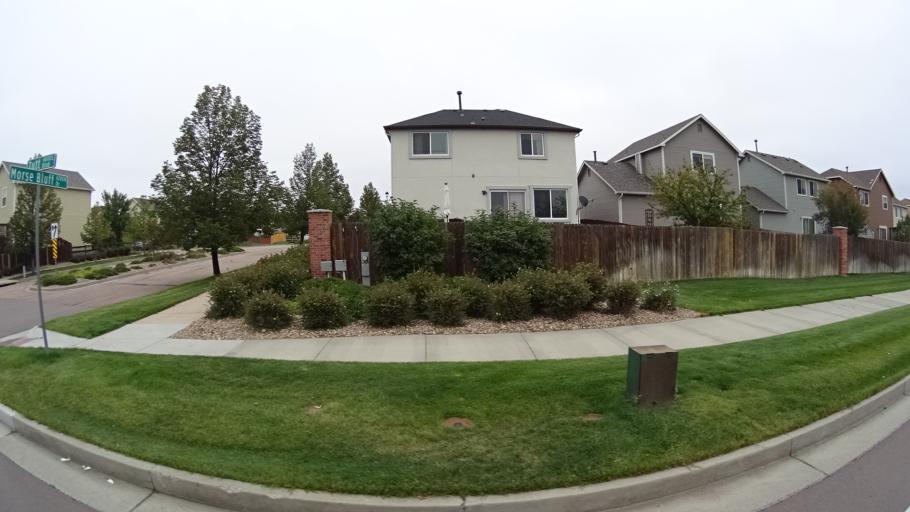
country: US
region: Colorado
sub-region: El Paso County
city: Cimarron Hills
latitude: 38.9210
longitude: -104.7171
